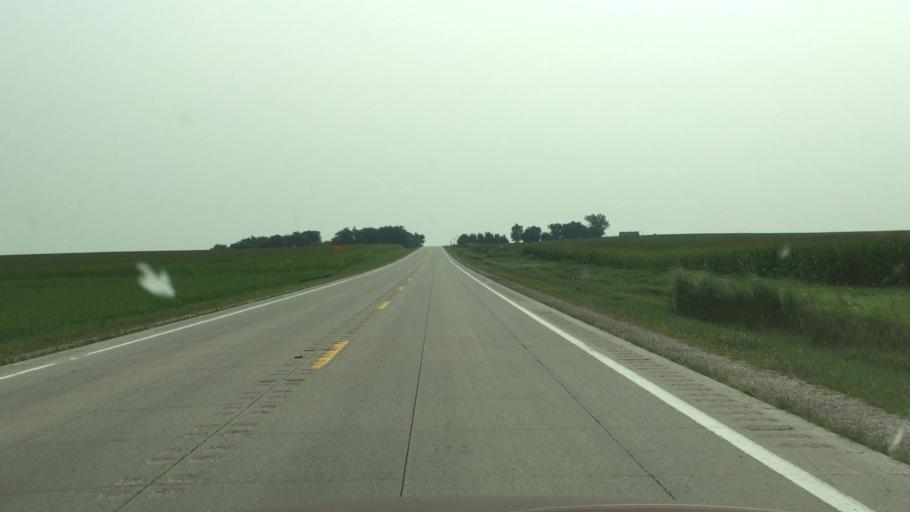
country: US
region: Iowa
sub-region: Osceola County
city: Sibley
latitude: 43.4327
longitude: -95.6703
